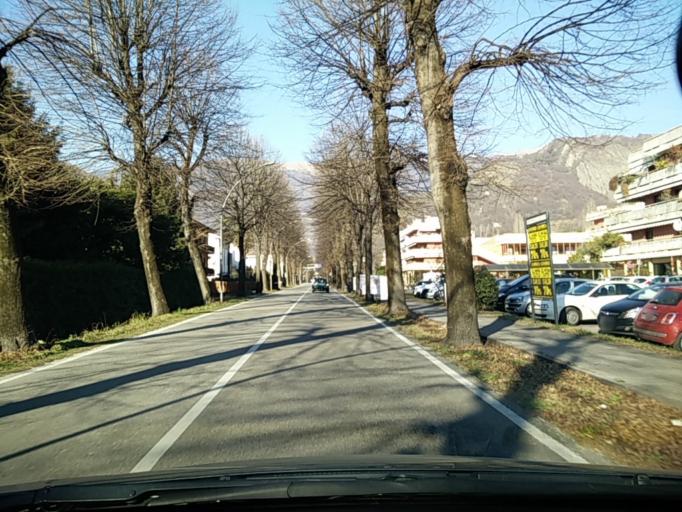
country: IT
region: Veneto
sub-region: Provincia di Treviso
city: Vittorio Veneto
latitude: 45.9927
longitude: 12.2971
